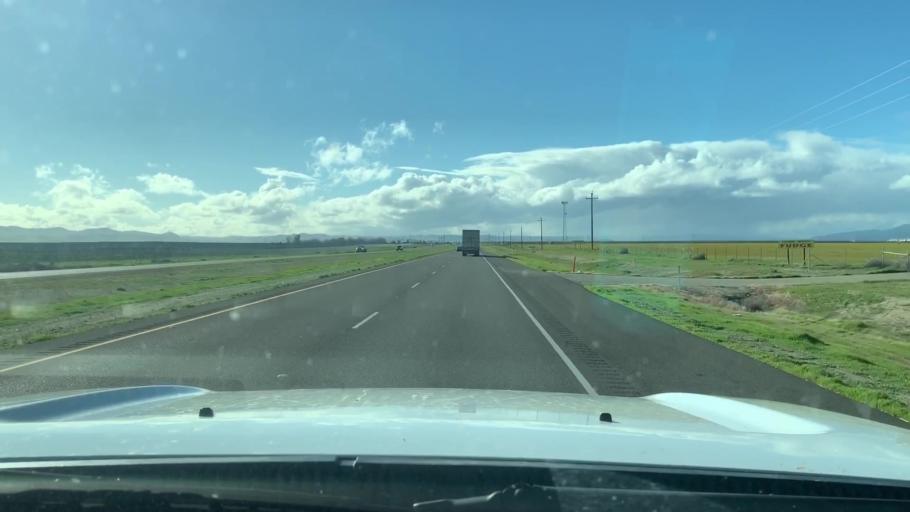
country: US
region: California
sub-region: Kern County
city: Lost Hills
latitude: 35.6157
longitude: -119.8407
